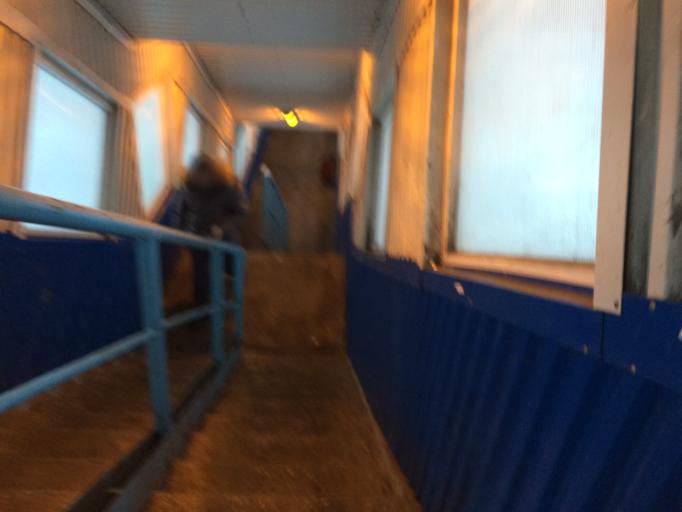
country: RU
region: Chelyabinsk
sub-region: Gorod Magnitogorsk
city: Magnitogorsk
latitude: 53.4030
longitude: 59.0452
